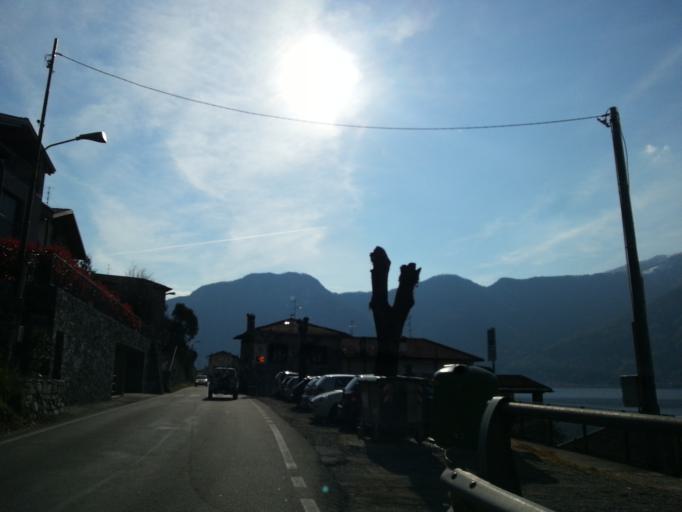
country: IT
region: Lombardy
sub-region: Provincia di Como
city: Ossuccio
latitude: 45.9683
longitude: 9.1777
